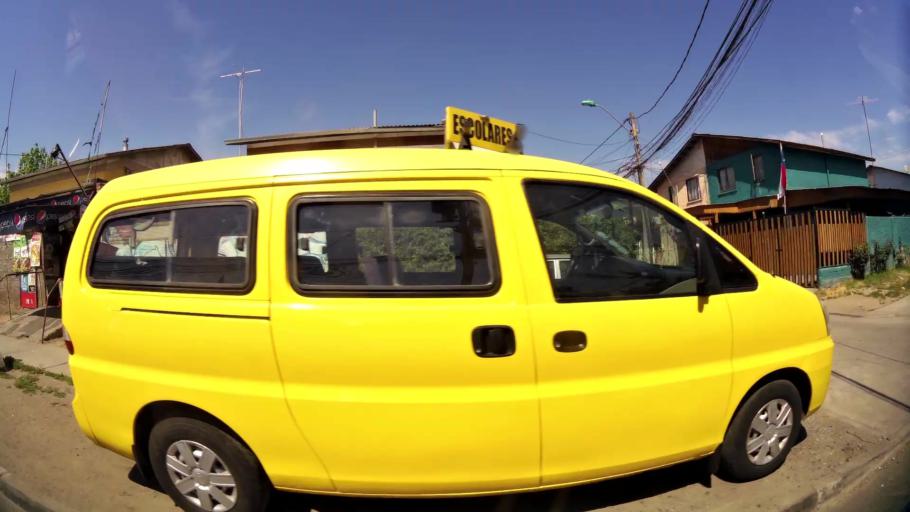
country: CL
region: Santiago Metropolitan
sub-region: Provincia de Talagante
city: Talagante
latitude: -33.6531
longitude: -70.9046
